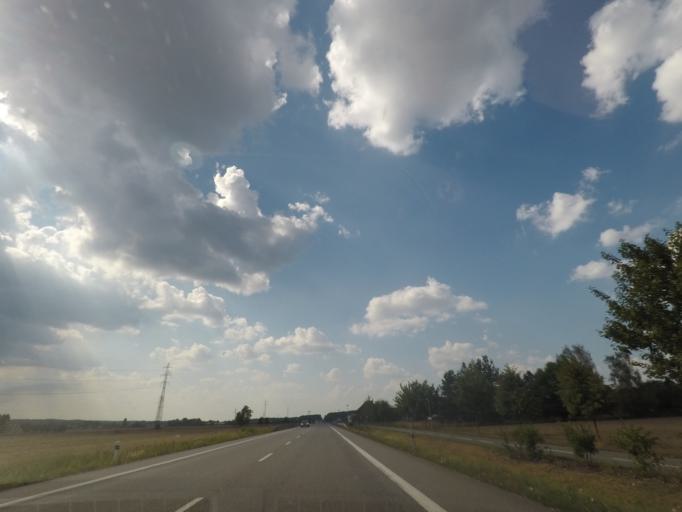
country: CZ
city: Albrechtice nad Orlici
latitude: 50.1662
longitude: 16.0480
